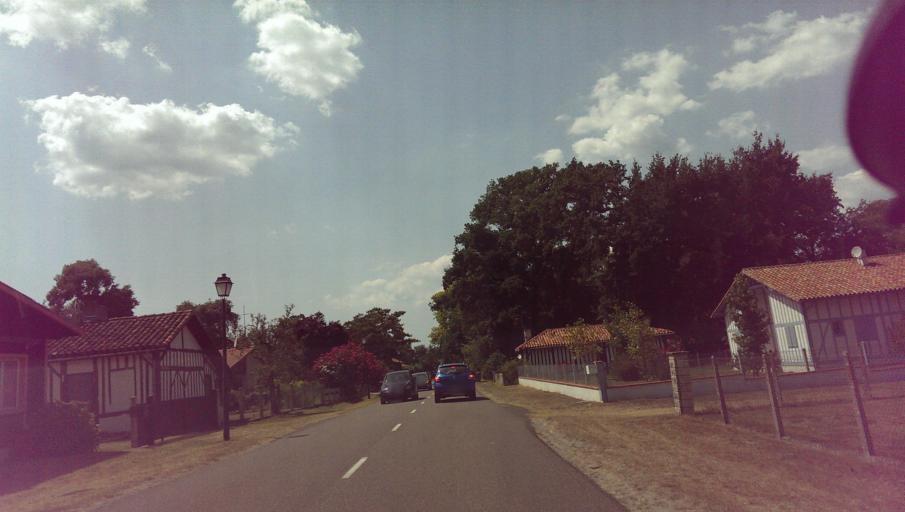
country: FR
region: Aquitaine
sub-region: Departement des Landes
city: Sabres
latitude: 44.1052
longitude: -0.5379
